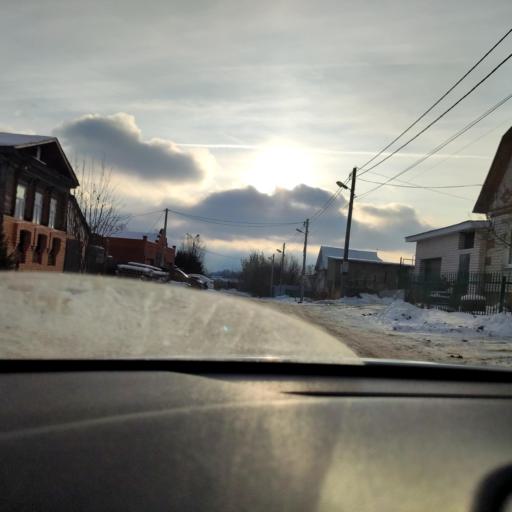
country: RU
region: Tatarstan
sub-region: Gorod Kazan'
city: Kazan
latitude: 55.7931
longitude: 49.0595
